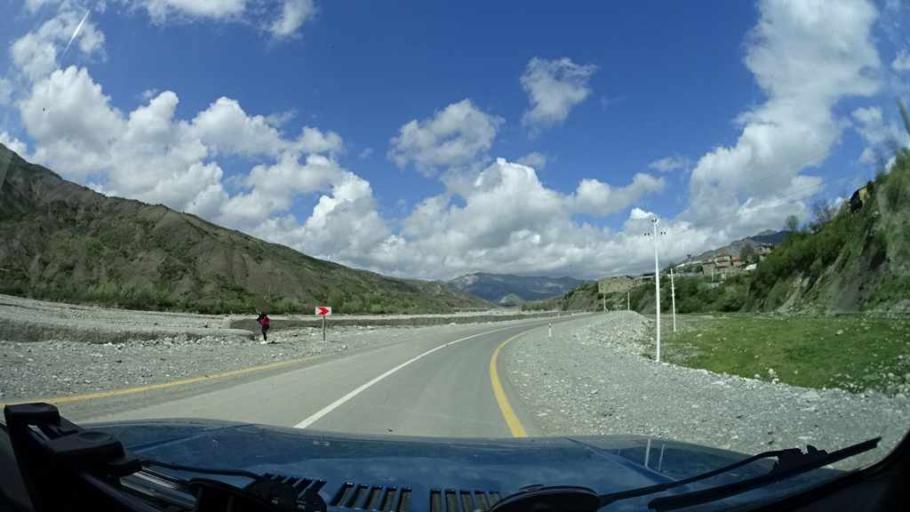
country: AZ
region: Ismayilli
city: Basqal
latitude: 40.8455
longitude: 48.3789
